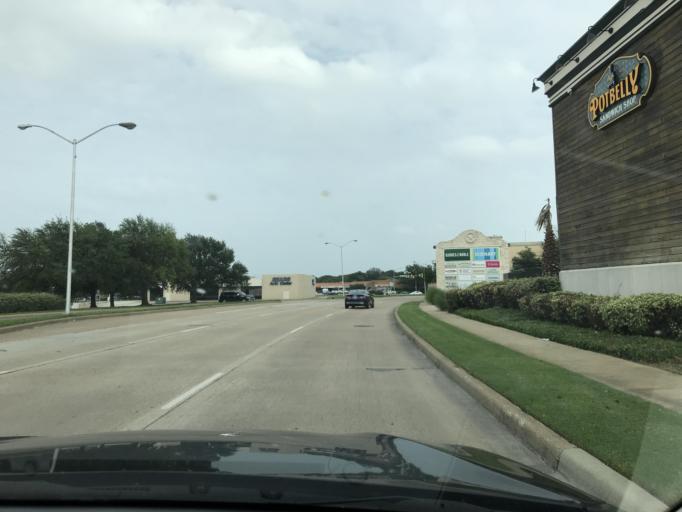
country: US
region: Texas
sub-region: Tarrant County
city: Edgecliff Village
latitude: 32.6760
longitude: -97.4002
